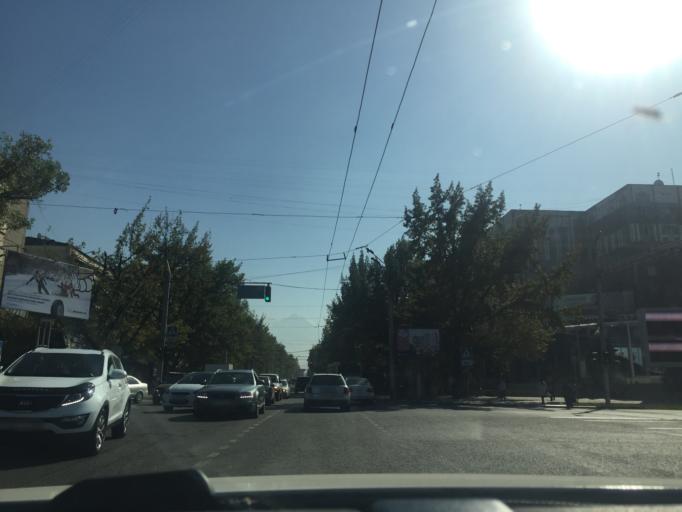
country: KZ
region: Almaty Qalasy
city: Almaty
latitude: 43.2522
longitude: 76.9023
